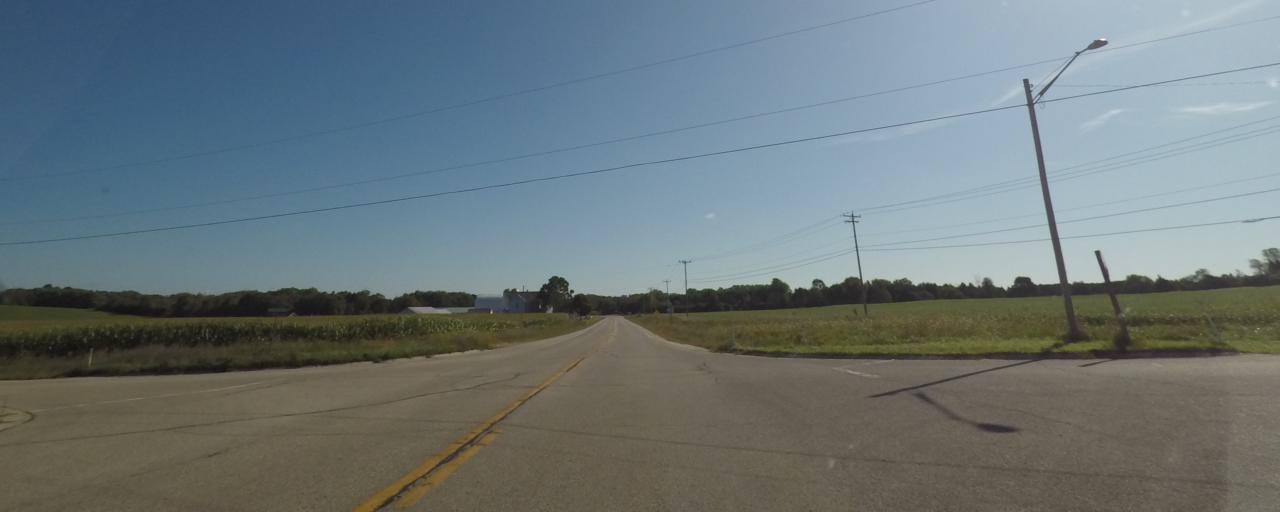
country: US
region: Wisconsin
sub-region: Waukesha County
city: Dousman
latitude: 43.0228
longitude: -88.5467
